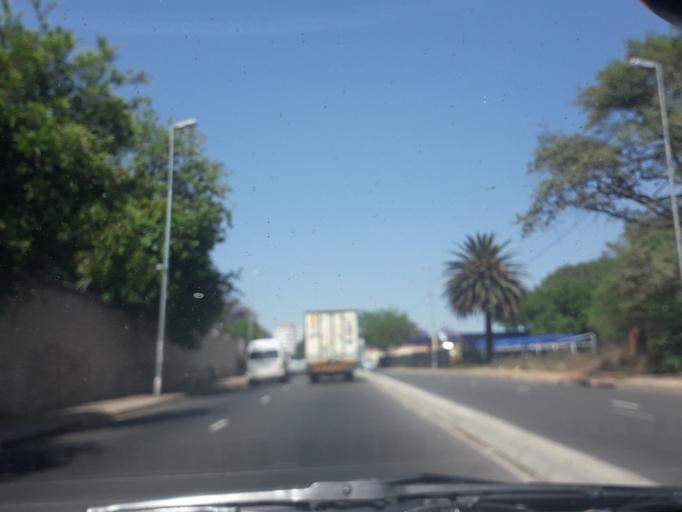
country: ZA
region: Gauteng
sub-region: City of Johannesburg Metropolitan Municipality
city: Johannesburg
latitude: -26.1734
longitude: 28.0685
